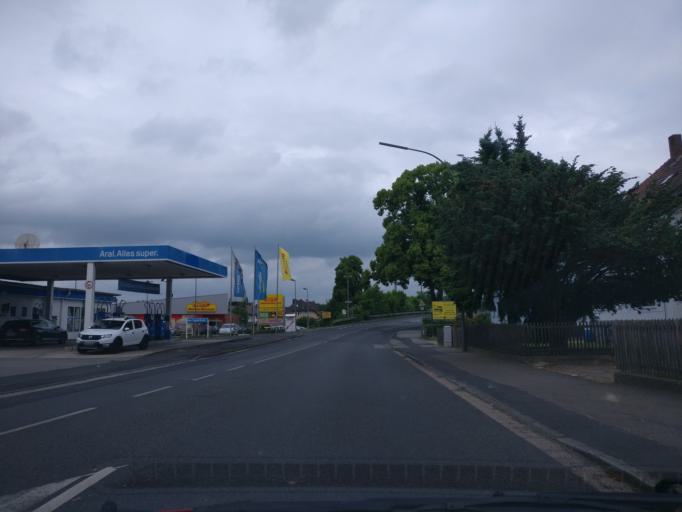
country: DE
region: Hesse
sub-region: Regierungsbezirk Kassel
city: Kassel
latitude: 51.3473
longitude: 9.5242
